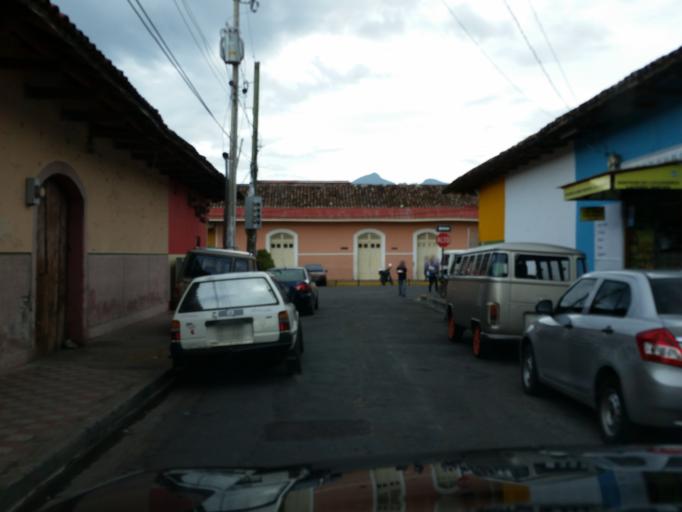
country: NI
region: Granada
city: Granada
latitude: 11.9305
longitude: -85.9513
